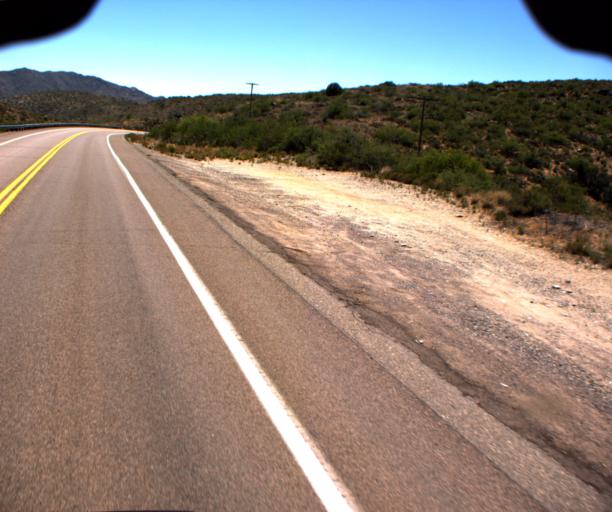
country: US
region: Arizona
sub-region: Yavapai County
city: Bagdad
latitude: 34.5441
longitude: -113.1472
